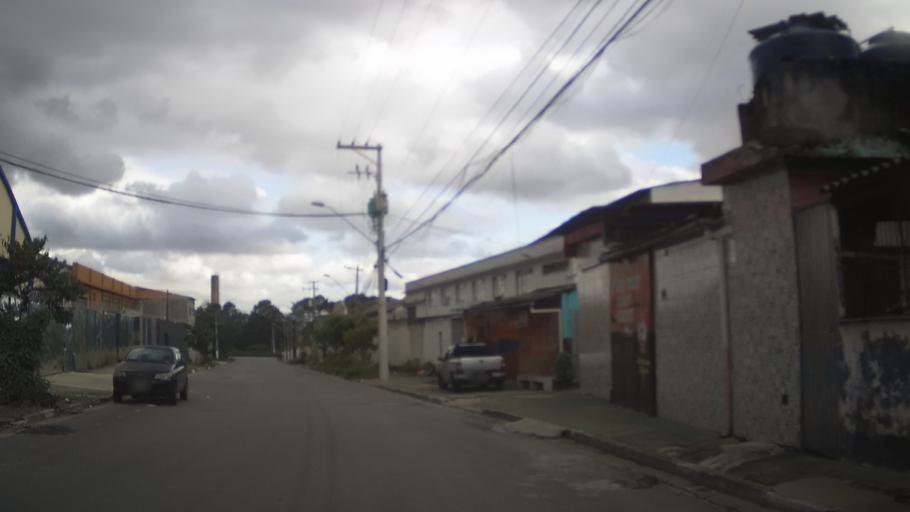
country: BR
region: Sao Paulo
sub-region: Guarulhos
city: Guarulhos
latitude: -23.4598
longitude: -46.4797
